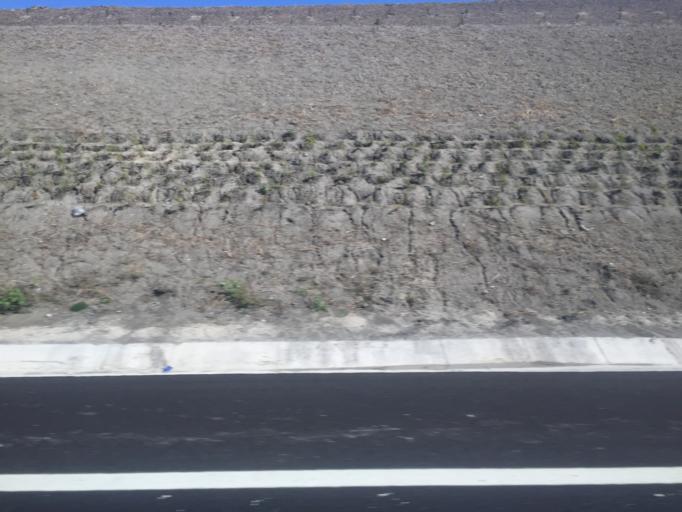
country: TR
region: Bursa
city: Mahmudiye
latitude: 40.2564
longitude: 28.7038
